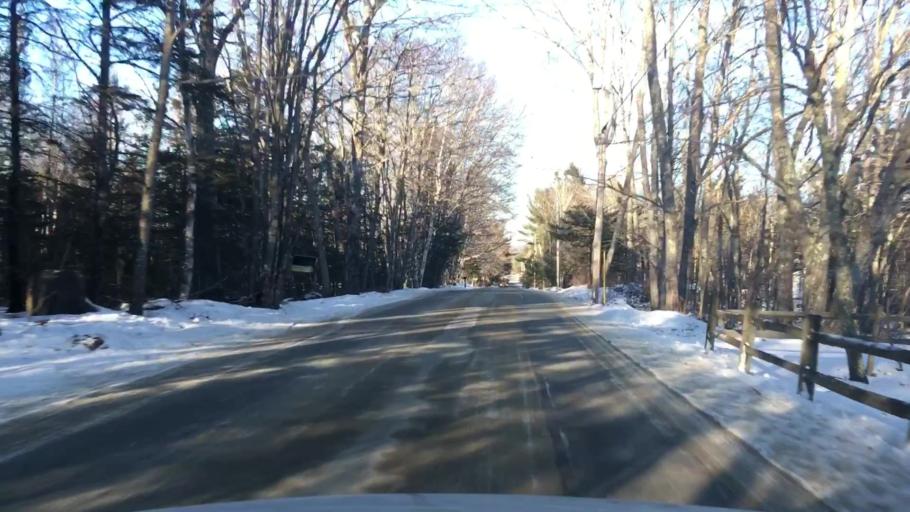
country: US
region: Maine
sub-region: Hancock County
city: Penobscot
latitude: 44.3880
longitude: -68.7172
